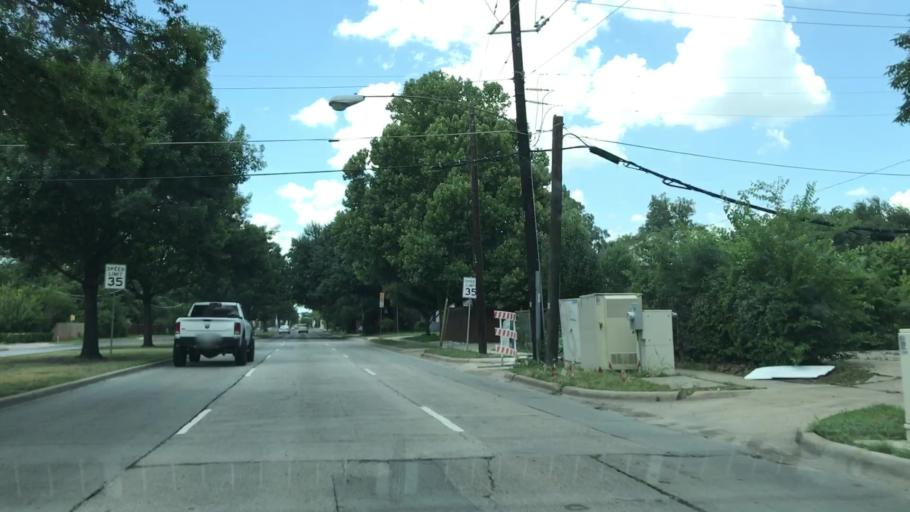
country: US
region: Texas
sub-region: Dallas County
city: University Park
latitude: 32.8667
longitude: -96.8560
